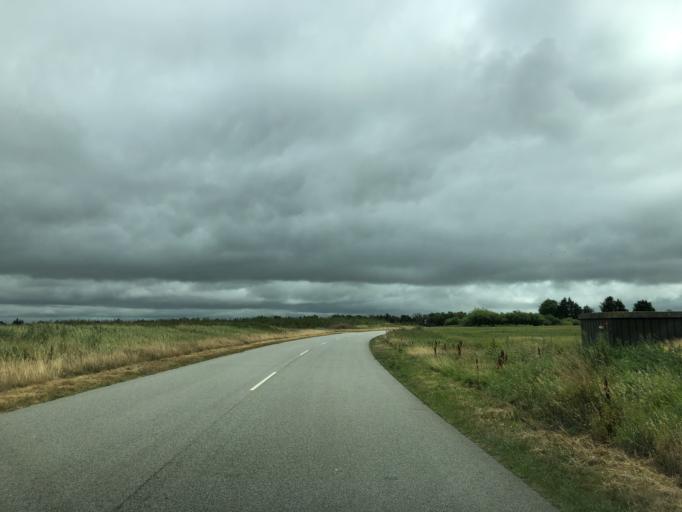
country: DK
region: Central Jutland
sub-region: Herning Kommune
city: Vildbjerg
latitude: 56.1854
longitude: 8.7542
